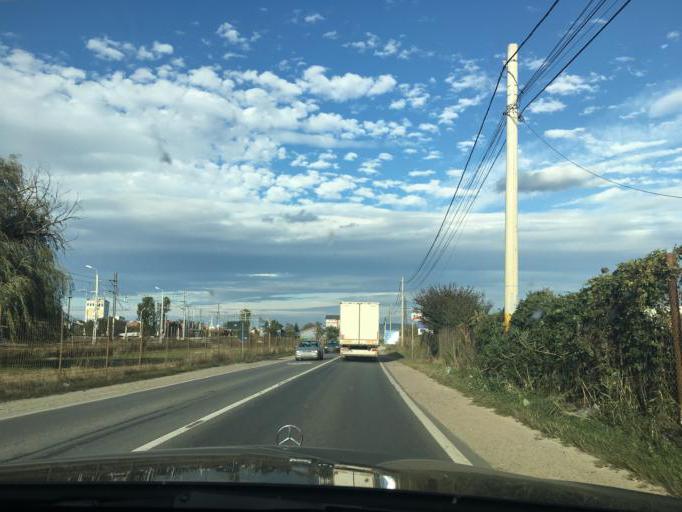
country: RO
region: Alba
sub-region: Municipiul Alba Iulia
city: Alba Iulia
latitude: 46.0513
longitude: 23.5700
